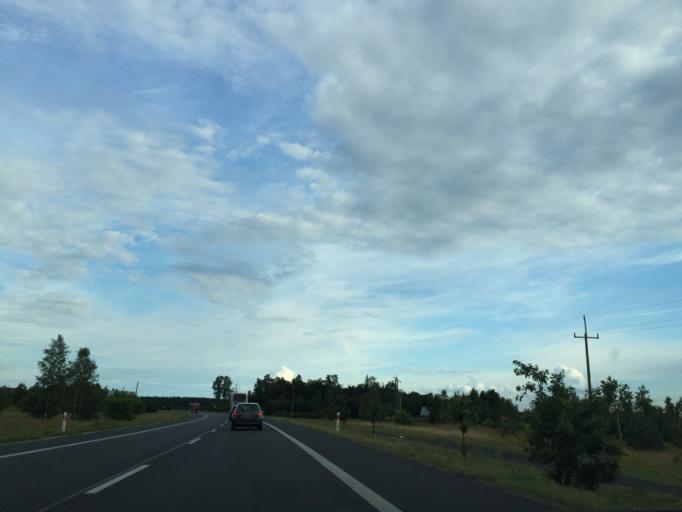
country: PL
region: Lublin Voivodeship
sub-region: Powiat lubartowski
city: Lubartow
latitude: 51.4566
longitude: 22.5759
